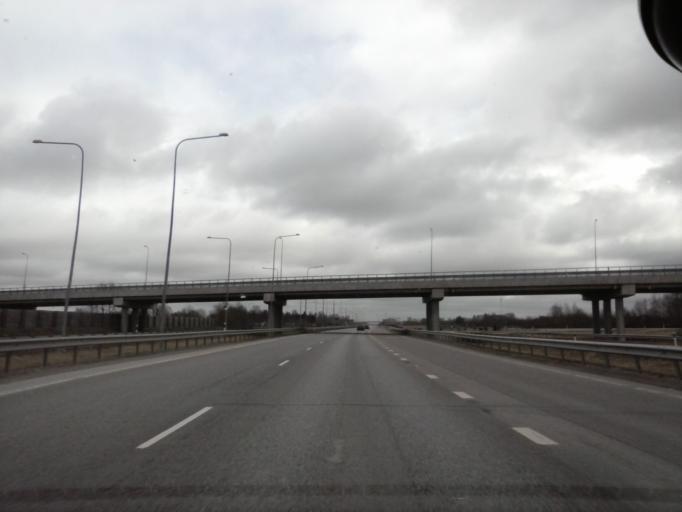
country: EE
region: Harju
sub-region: Rae vald
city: Vaida
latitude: 59.2908
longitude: 24.9655
